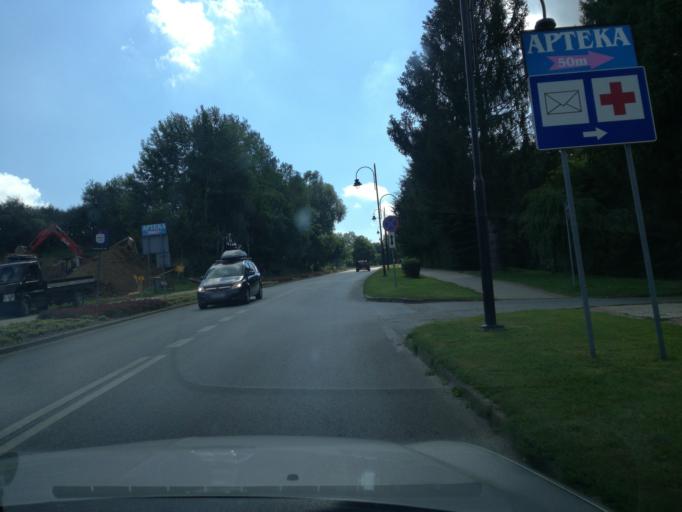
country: PL
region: Subcarpathian Voivodeship
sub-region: Powiat leski
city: Polanczyk
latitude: 49.3706
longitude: 22.4275
